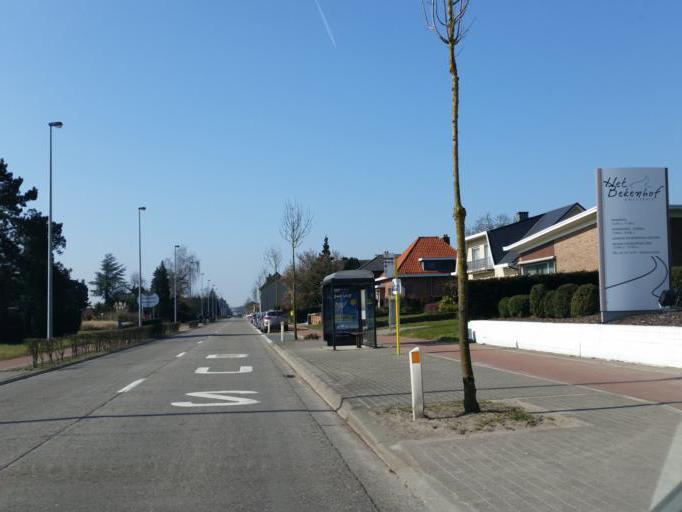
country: BE
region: Flanders
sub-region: Provincie Oost-Vlaanderen
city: Temse
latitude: 51.1286
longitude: 4.2397
